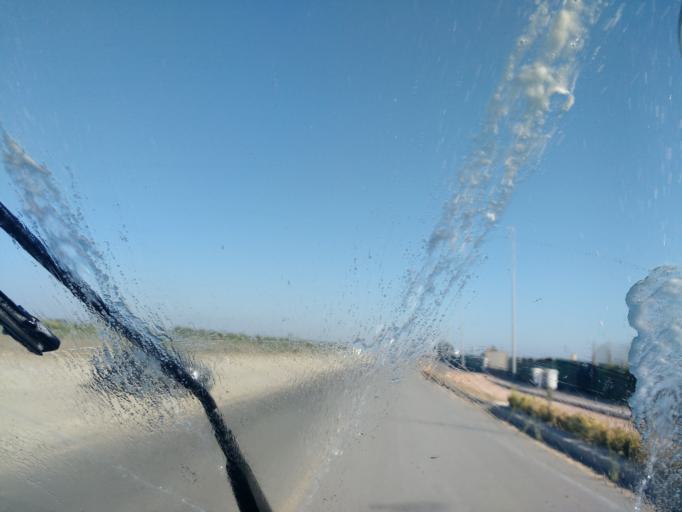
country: IT
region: Latium
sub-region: Citta metropolitana di Roma Capitale
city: Passo Oscuro
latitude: 41.8916
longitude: 12.1656
